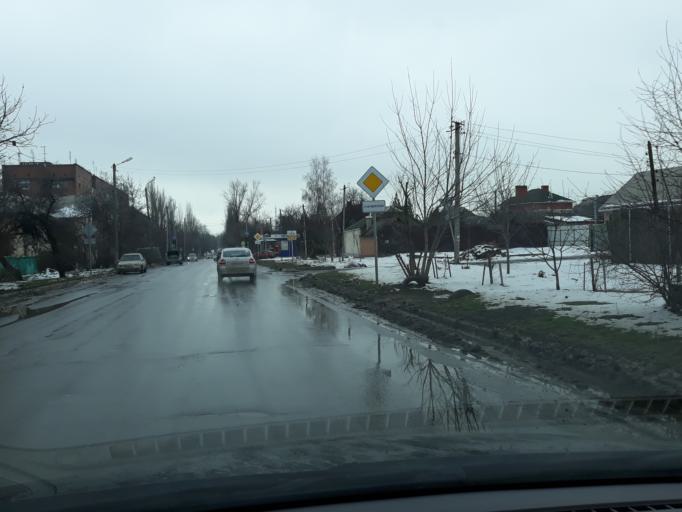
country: RU
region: Rostov
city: Taganrog
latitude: 47.2259
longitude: 38.9008
